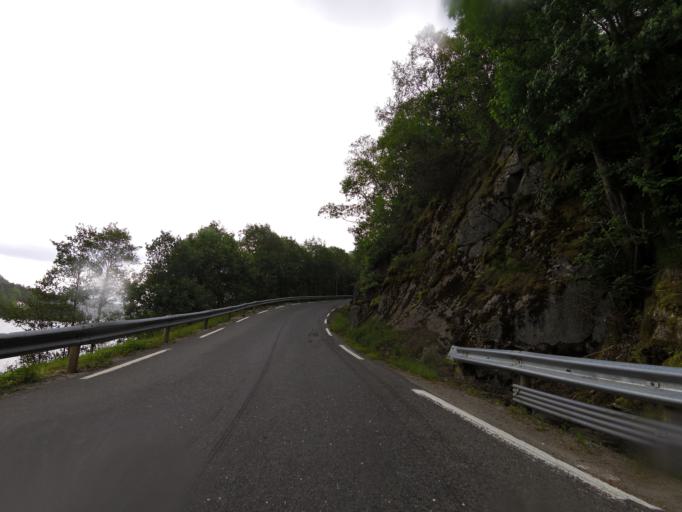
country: NO
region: Vest-Agder
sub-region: Lyngdal
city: Lyngdal
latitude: 58.1121
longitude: 7.0806
